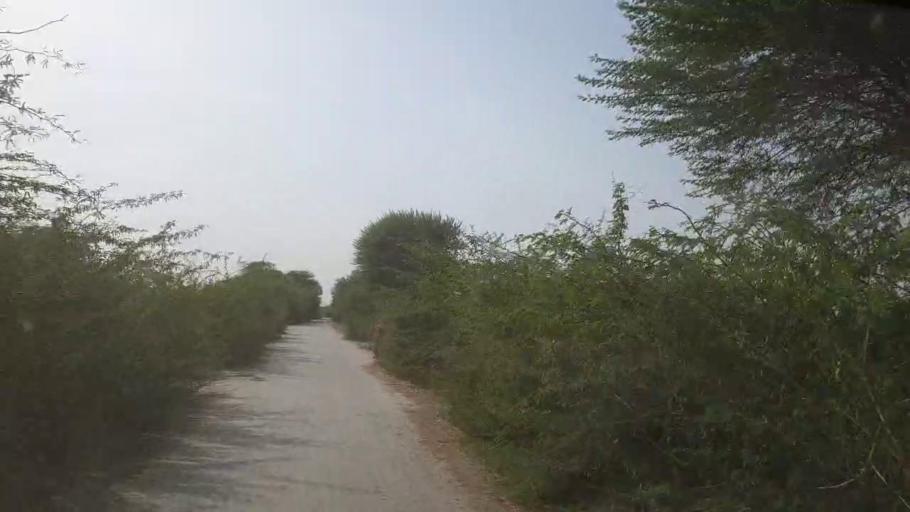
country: PK
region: Sindh
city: Nabisar
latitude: 25.0413
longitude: 69.4944
